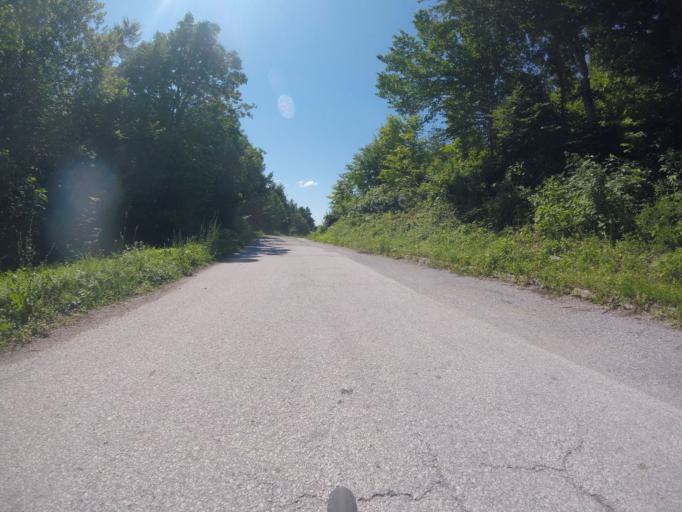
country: SI
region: Kostanjevica na Krki
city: Kostanjevica na Krki
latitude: 45.7963
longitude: 15.4956
